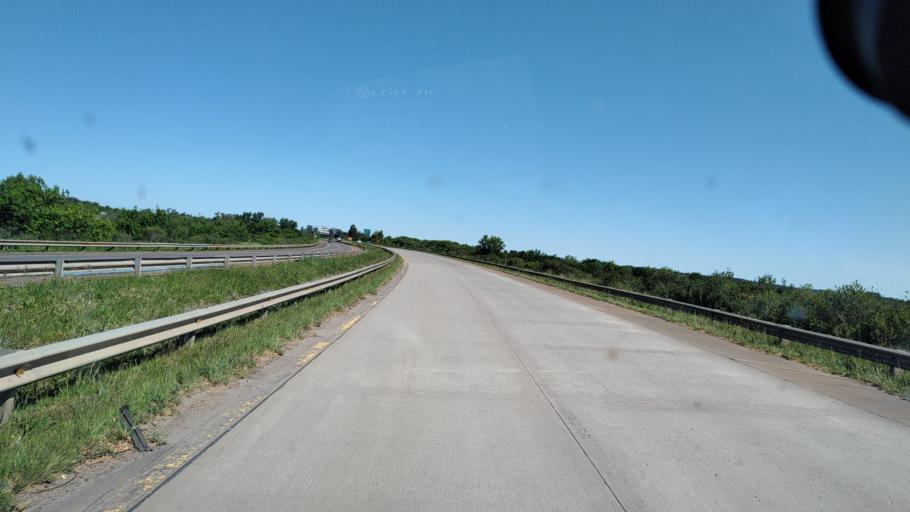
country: AR
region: Entre Rios
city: Colon
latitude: -32.1630
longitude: -58.2401
